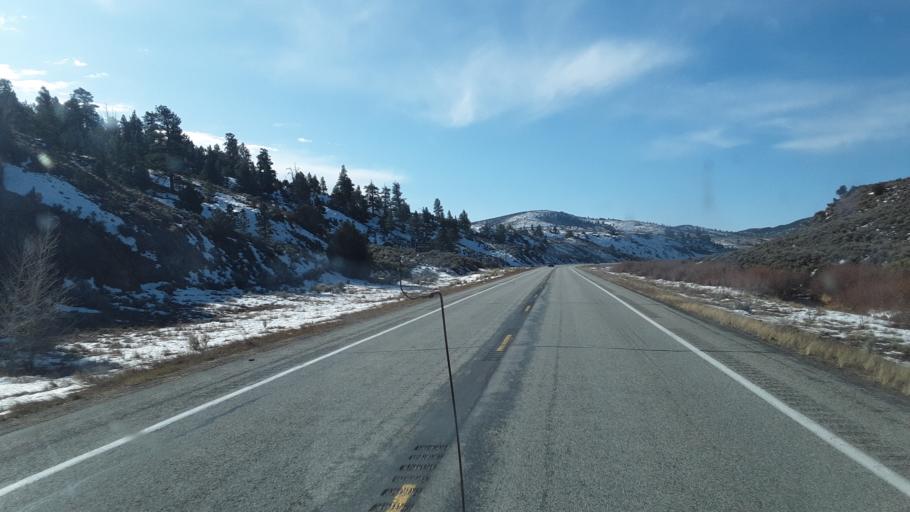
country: US
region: Colorado
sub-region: Costilla County
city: San Luis
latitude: 37.5206
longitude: -105.2996
